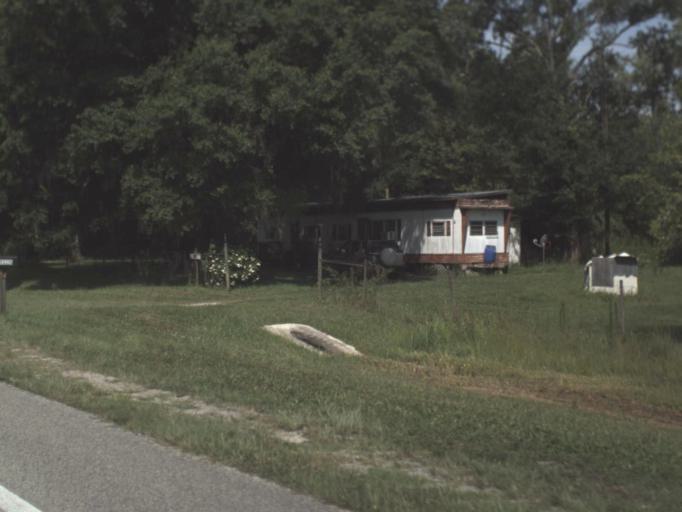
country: US
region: Florida
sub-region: Alachua County
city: Waldo
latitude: 29.7784
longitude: -82.1834
